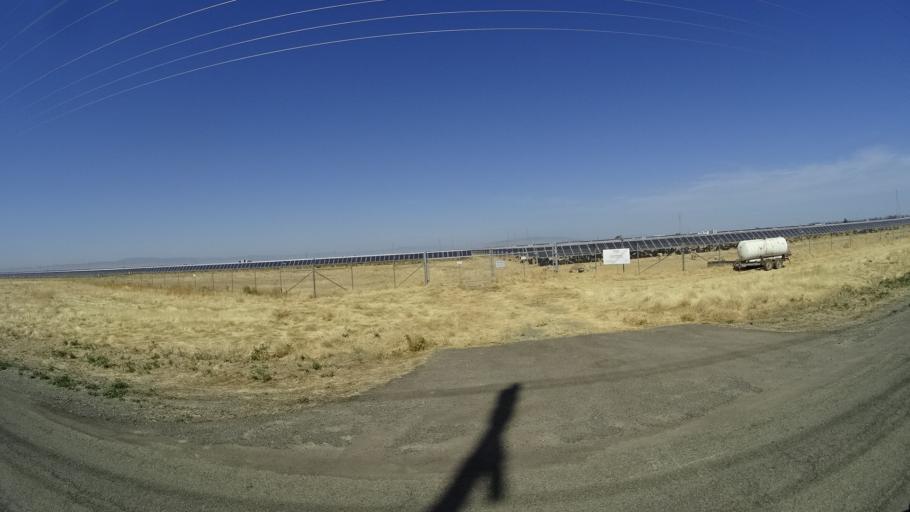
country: US
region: California
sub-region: Kings County
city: Lemoore Station
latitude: 36.2309
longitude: -119.9052
